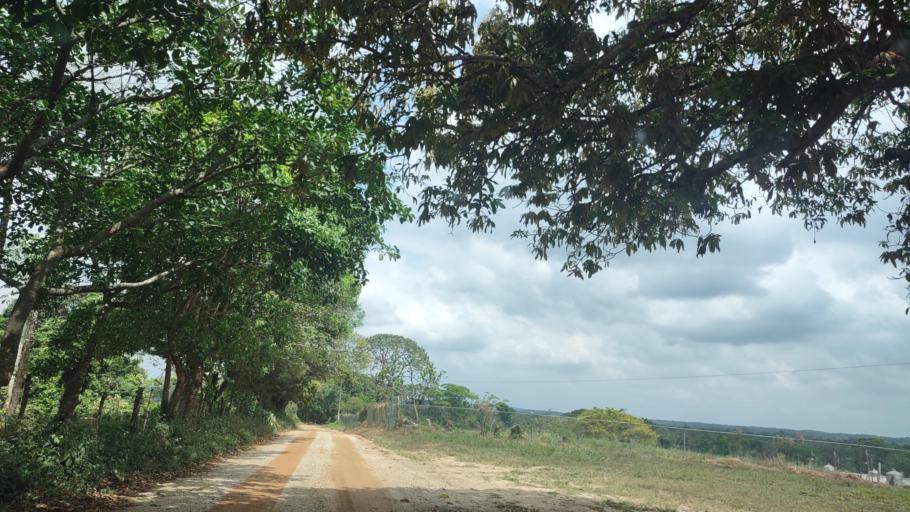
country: MX
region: Veracruz
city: Las Choapas
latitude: 17.9580
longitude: -94.1157
